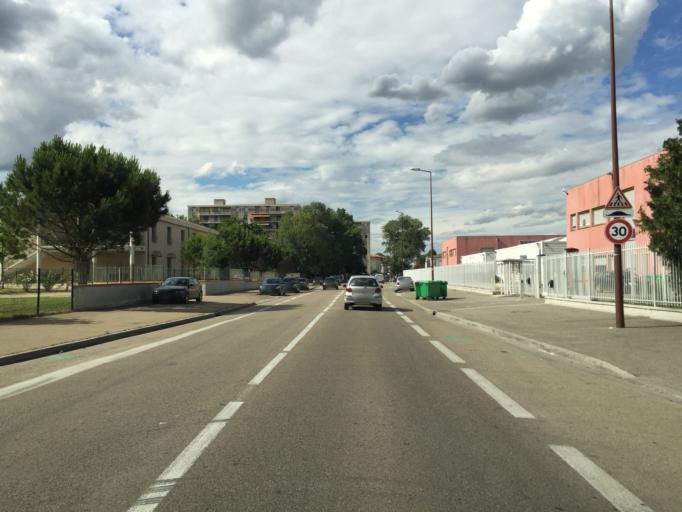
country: FR
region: Provence-Alpes-Cote d'Azur
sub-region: Departement du Vaucluse
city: Avignon
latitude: 43.9244
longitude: 4.8041
